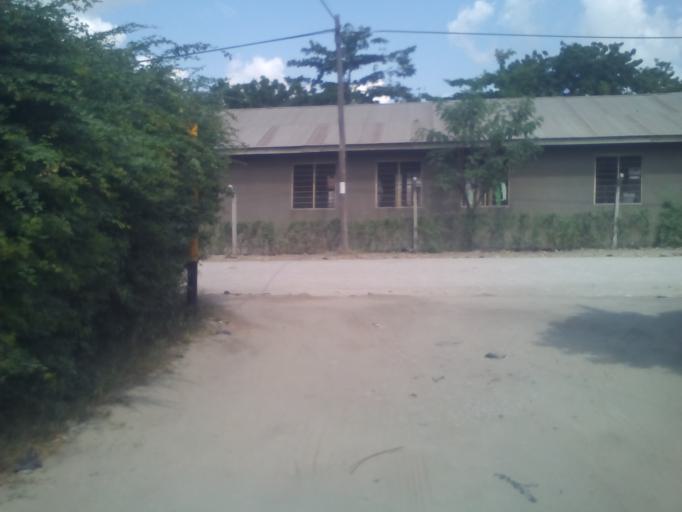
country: TZ
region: Dar es Salaam
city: Dar es Salaam
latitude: -6.8474
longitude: 39.2753
